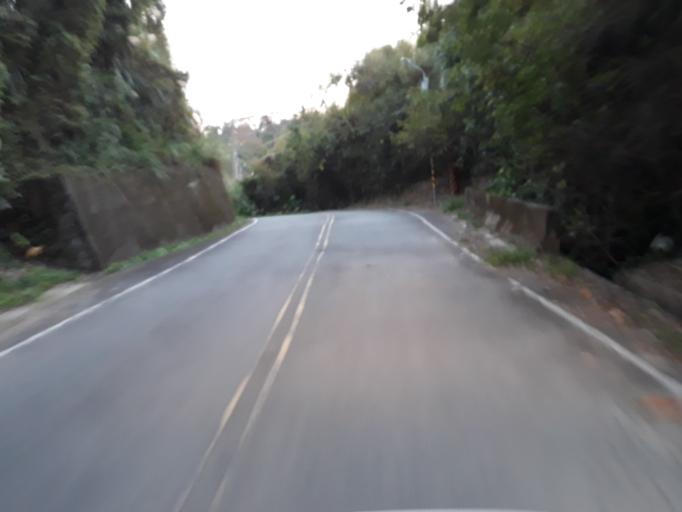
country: TW
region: Taiwan
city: Fengyuan
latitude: 24.3586
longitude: 120.8634
